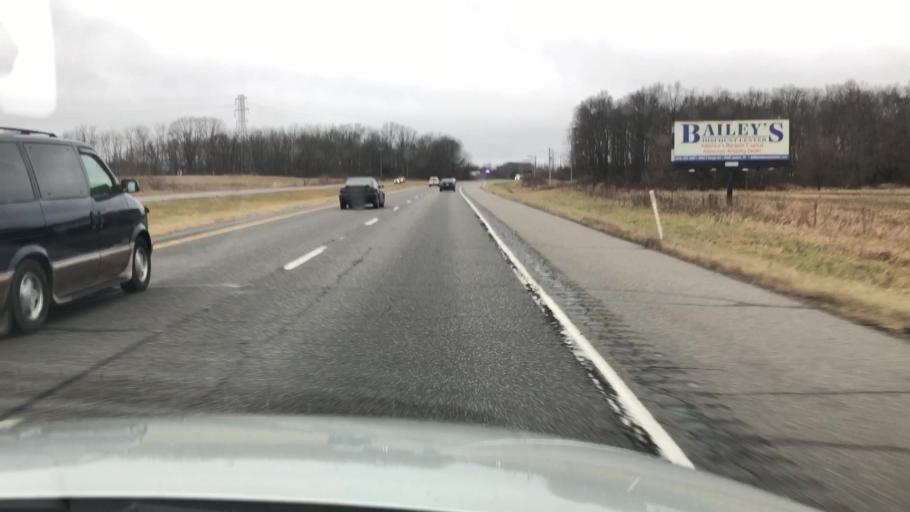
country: US
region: Indiana
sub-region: Marshall County
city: Plymouth
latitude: 41.3615
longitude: -86.3631
